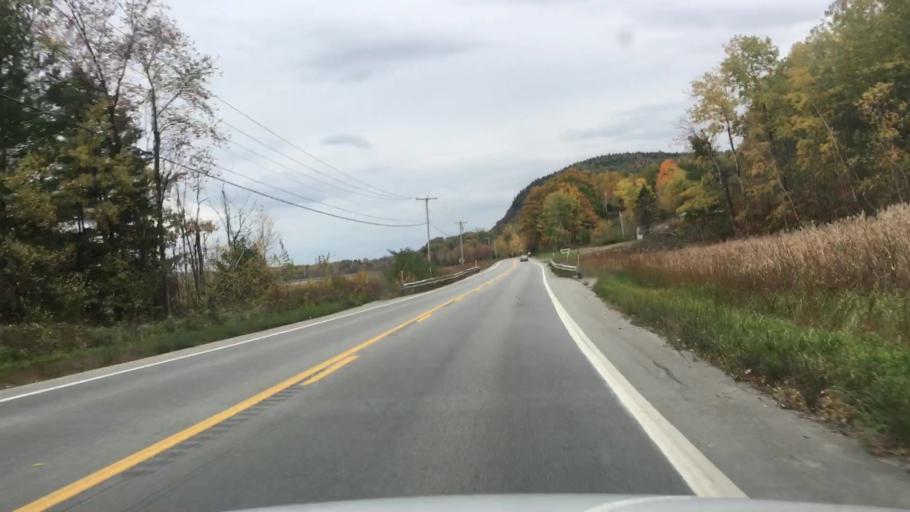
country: US
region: Maine
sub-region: Waldo County
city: Frankfort
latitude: 44.5967
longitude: -68.8655
